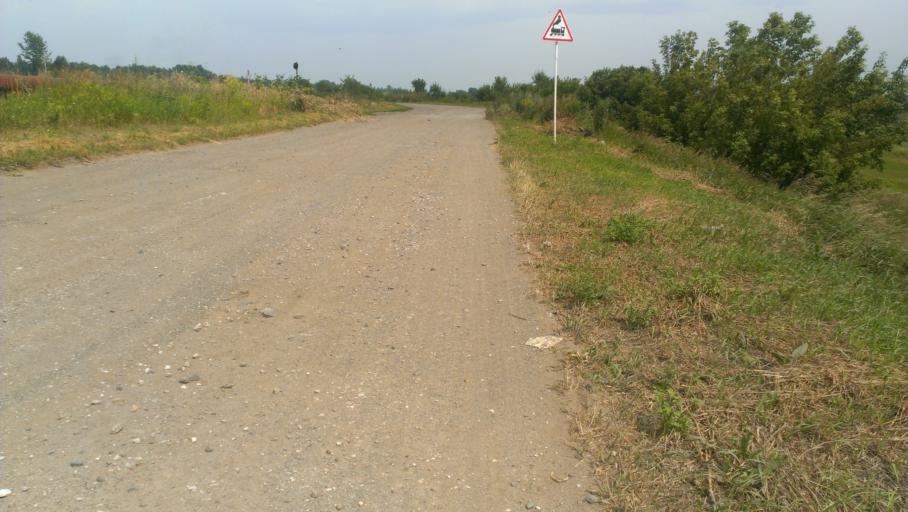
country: RU
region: Altai Krai
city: Gon'ba
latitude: 53.3811
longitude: 83.6283
